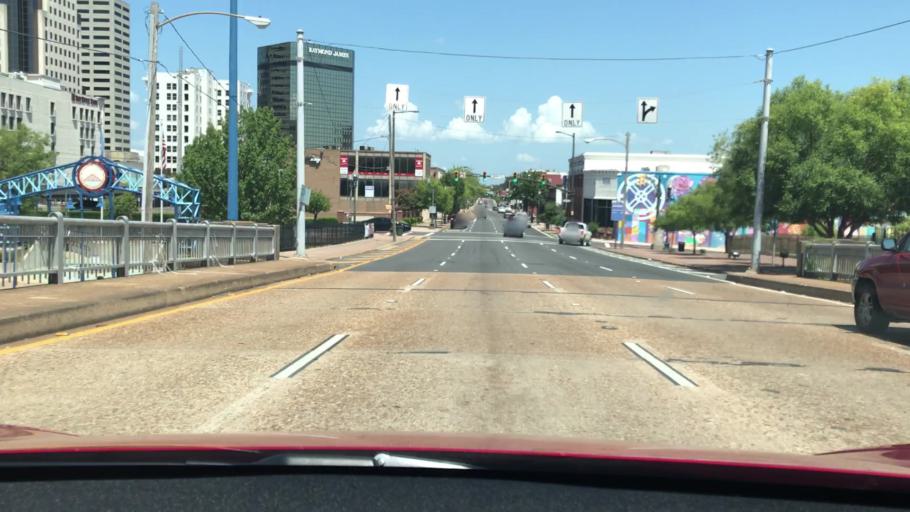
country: US
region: Louisiana
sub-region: Bossier Parish
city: Bossier City
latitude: 32.5128
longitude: -93.7446
